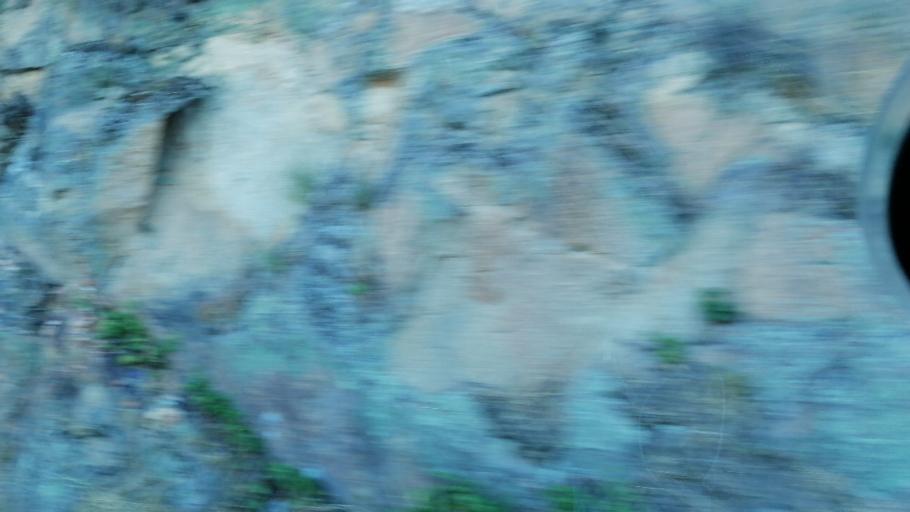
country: PT
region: Viseu
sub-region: Sao Joao da Pesqueira
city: Sao Joao da Pesqueira
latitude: 41.2266
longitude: -7.4238
